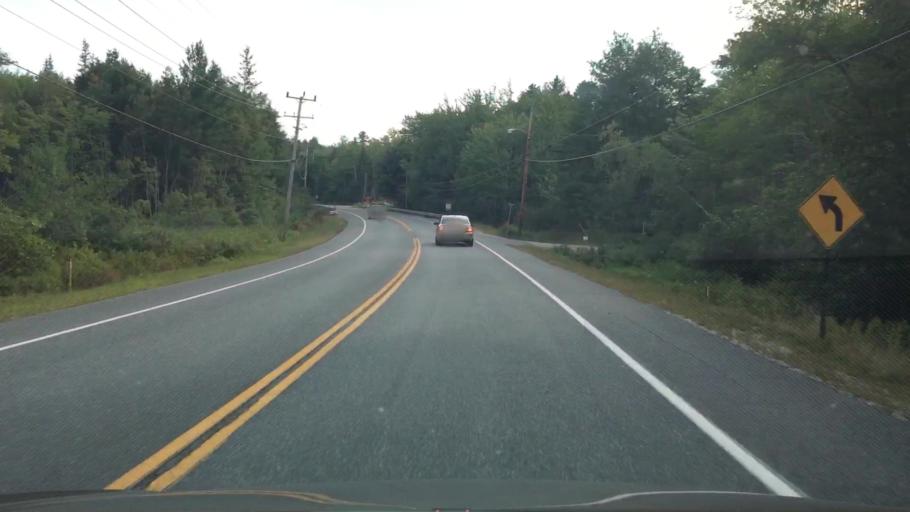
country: US
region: Maine
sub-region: Hancock County
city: Surry
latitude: 44.4417
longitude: -68.5681
